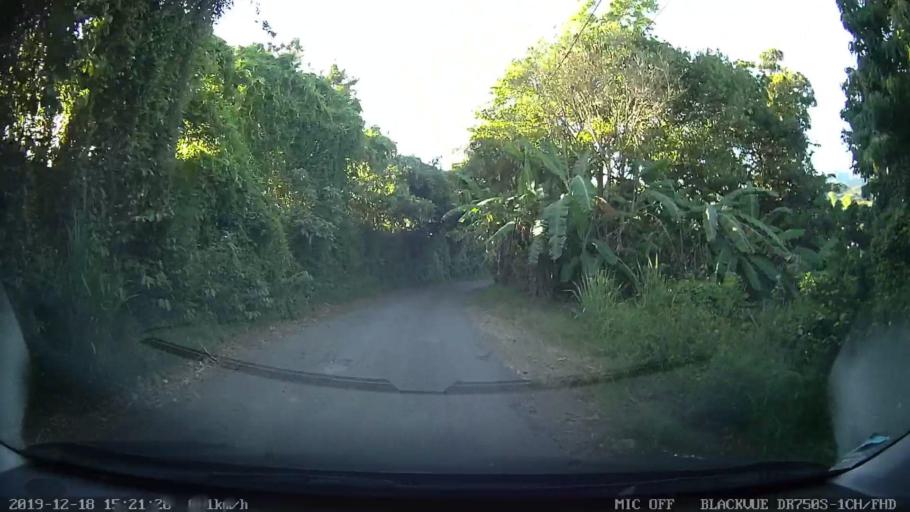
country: RE
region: Reunion
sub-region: Reunion
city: Bras-Panon
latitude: -20.9952
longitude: 55.6632
